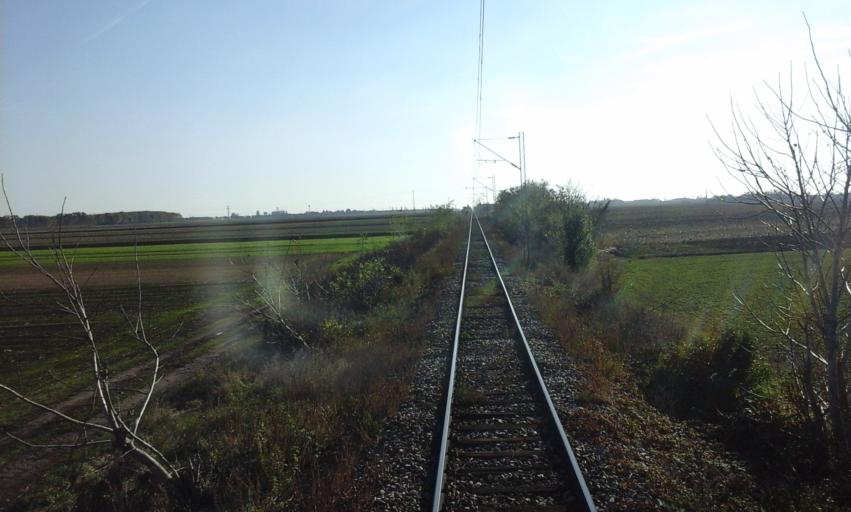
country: RS
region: Autonomna Pokrajina Vojvodina
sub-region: Severnobacki Okrug
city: Backa Topola
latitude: 45.7996
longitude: 19.6472
